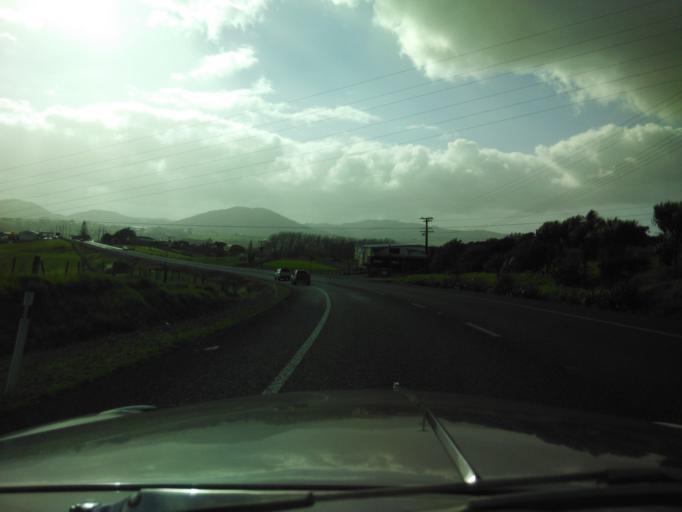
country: NZ
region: Auckland
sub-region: Auckland
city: Wellsford
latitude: -36.1754
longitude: 174.4493
